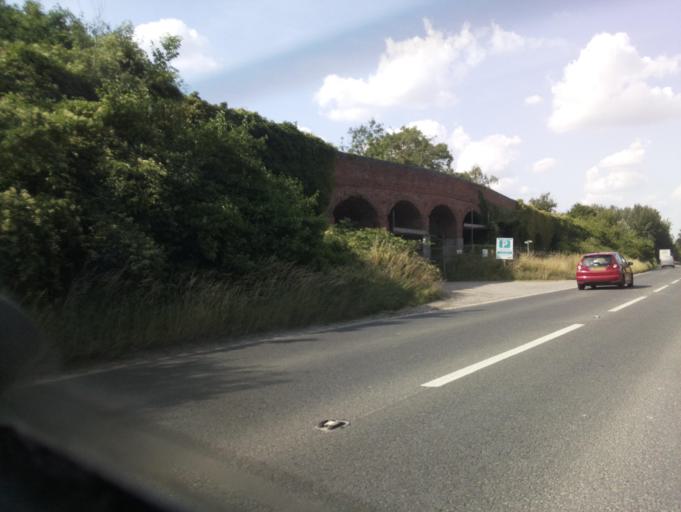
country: GB
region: England
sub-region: Wiltshire
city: Leigh
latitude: 51.6651
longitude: -1.9093
